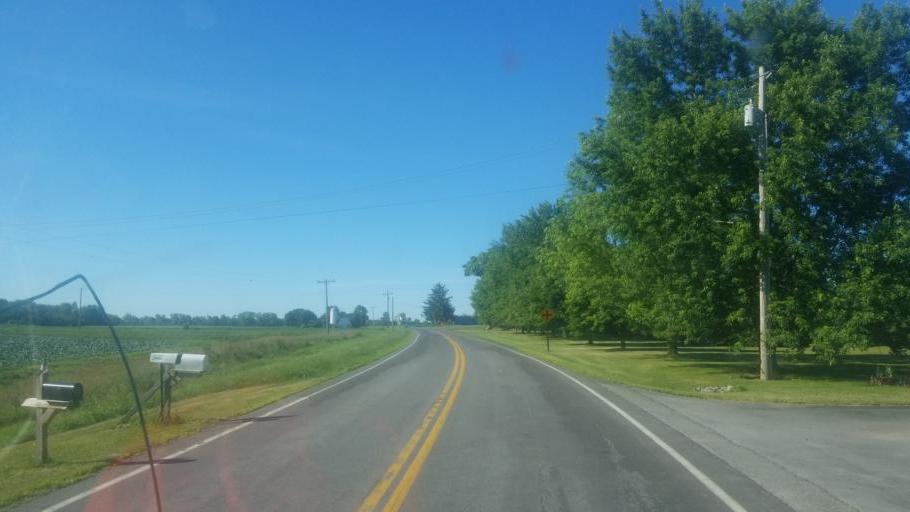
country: US
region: New York
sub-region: Ontario County
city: Clifton Springs
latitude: 42.8413
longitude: -77.1128
